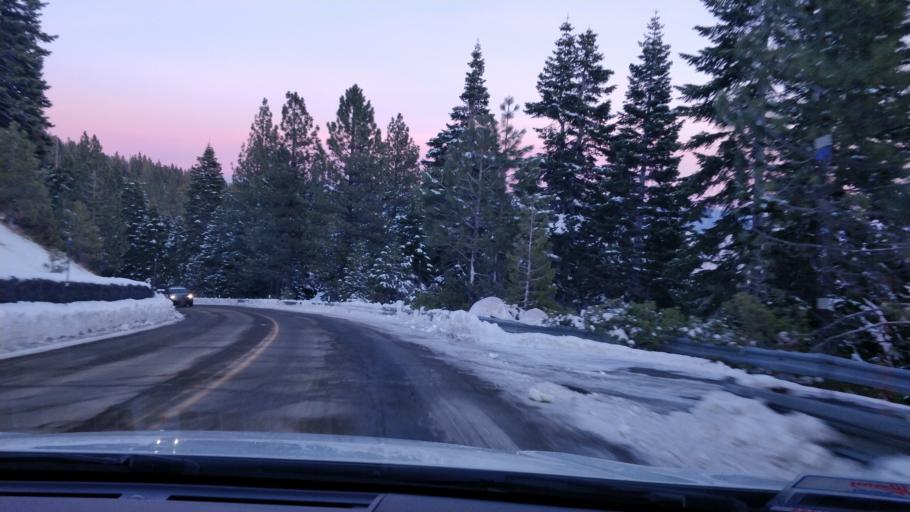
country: US
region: California
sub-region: Placer County
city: Sunnyside-Tahoe City
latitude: 39.1426
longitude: -120.1630
